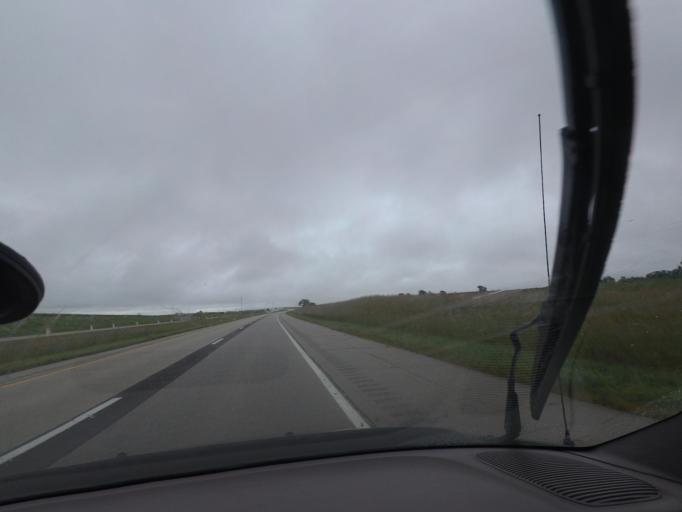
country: US
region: Illinois
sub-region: Sangamon County
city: Riverton
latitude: 39.8395
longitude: -89.3646
